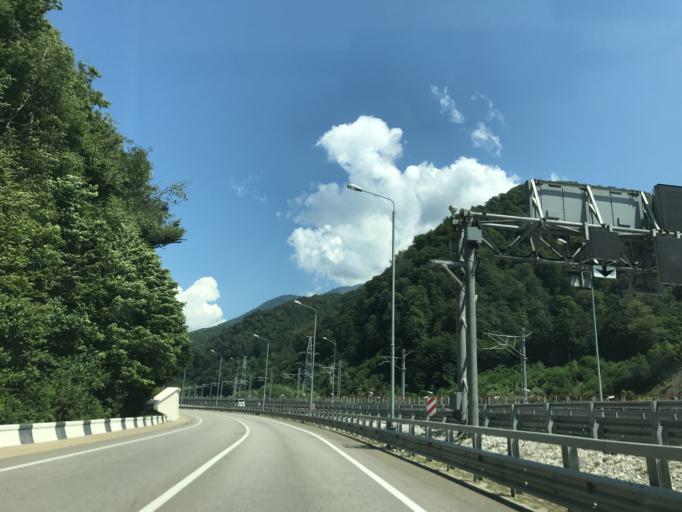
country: RU
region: Krasnodarskiy
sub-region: Sochi City
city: Krasnaya Polyana
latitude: 43.6454
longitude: 40.1358
